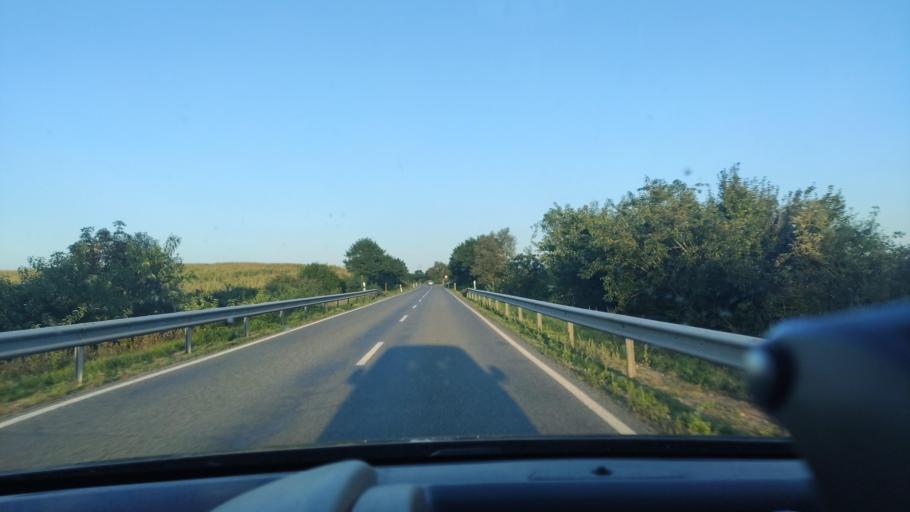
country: DE
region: Mecklenburg-Vorpommern
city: Krakow am See
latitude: 53.6168
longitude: 12.4028
